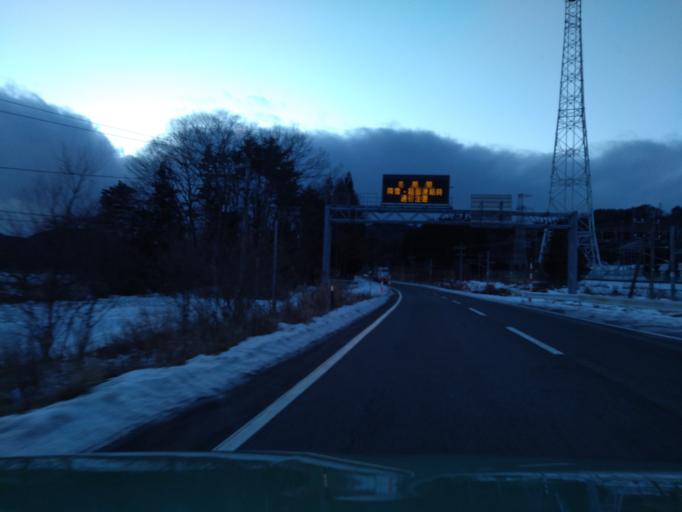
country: JP
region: Iwate
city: Shizukuishi
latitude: 39.6922
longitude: 140.9309
